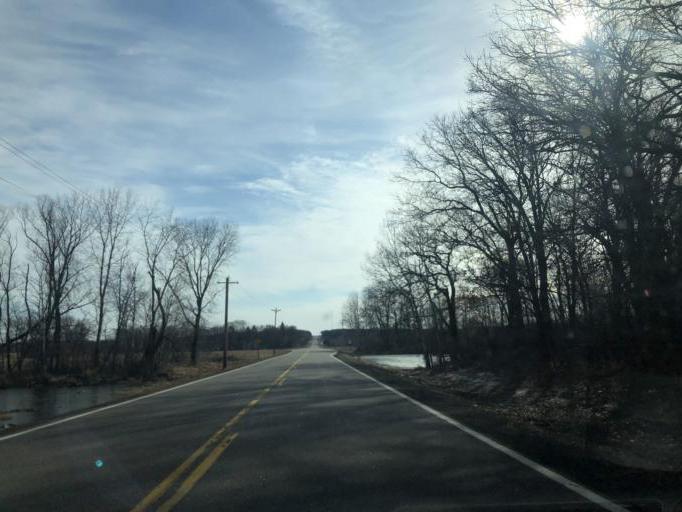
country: US
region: Minnesota
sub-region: Sherburne County
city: Becker
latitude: 45.4298
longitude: -93.8639
